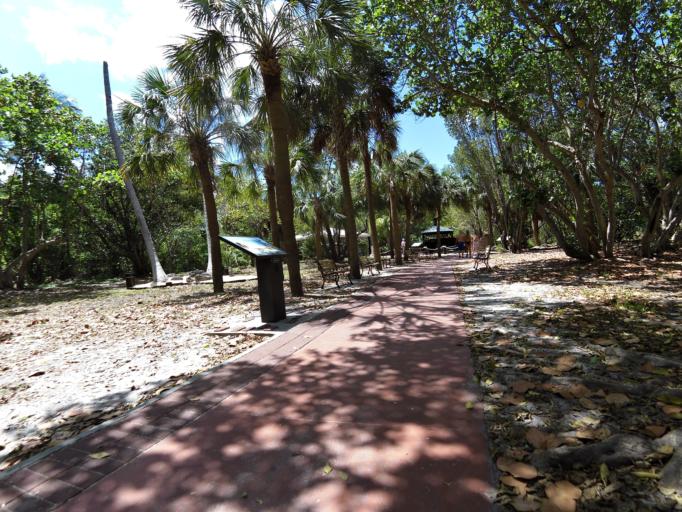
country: US
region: Florida
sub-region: Miami-Dade County
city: Key Biscayne
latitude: 25.6673
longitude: -80.1569
